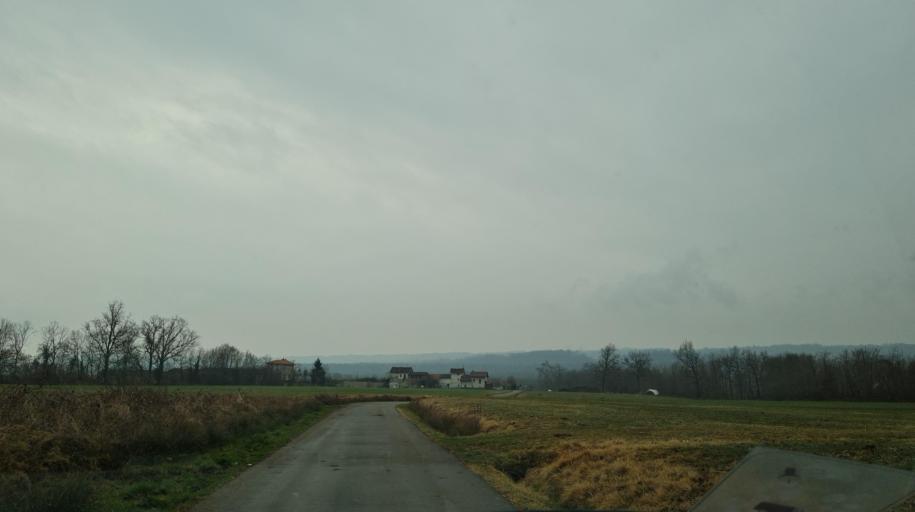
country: IT
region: Piedmont
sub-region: Provincia di Biella
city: Borriana
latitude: 45.5152
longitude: 8.0277
